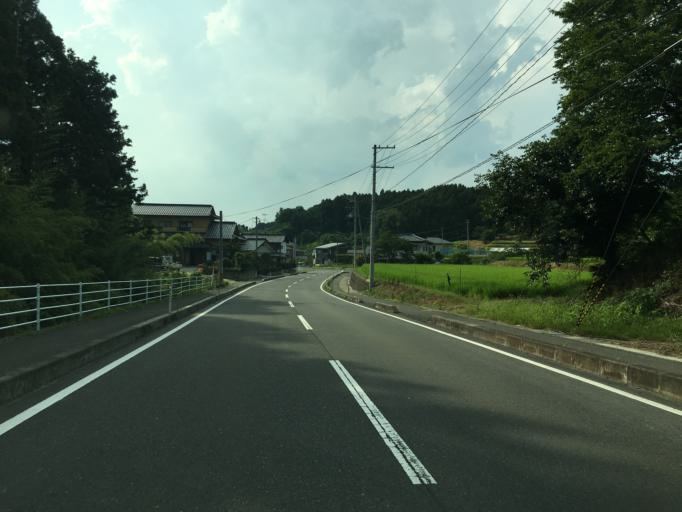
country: JP
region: Fukushima
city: Miharu
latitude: 37.4455
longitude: 140.4368
